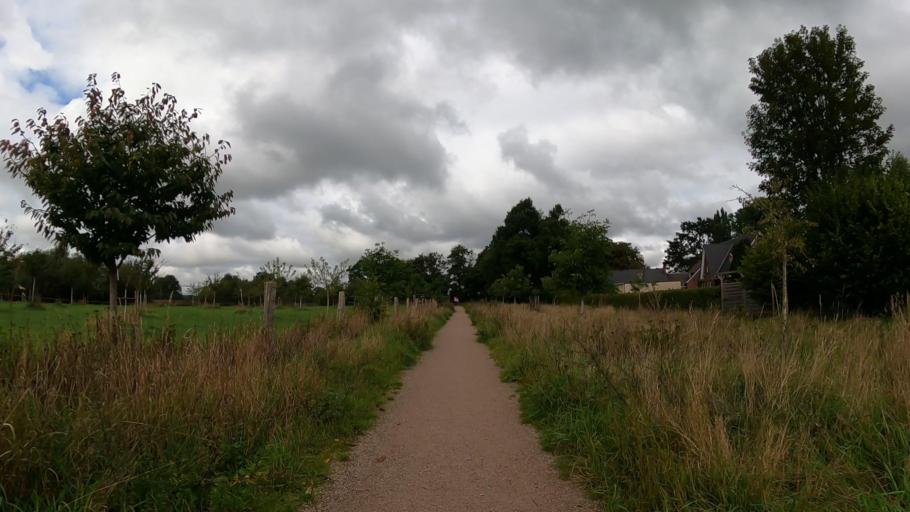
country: DE
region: Lower Saxony
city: Neu Wulmstorf
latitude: 53.4814
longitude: 9.8565
